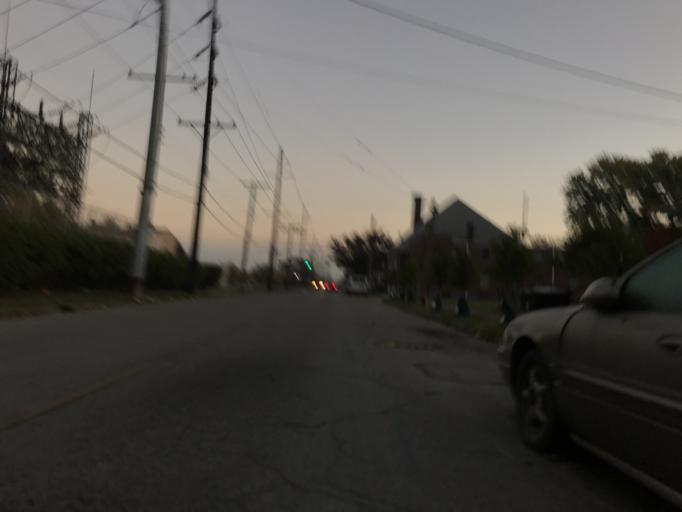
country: US
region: Kentucky
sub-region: Jefferson County
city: Louisville
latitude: 38.2391
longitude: -85.7425
